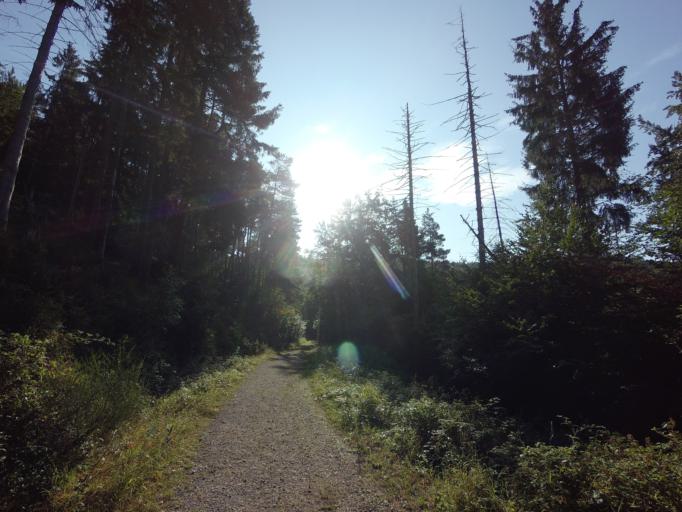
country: DE
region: North Rhine-Westphalia
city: Heimbach
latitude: 50.6146
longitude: 6.4070
